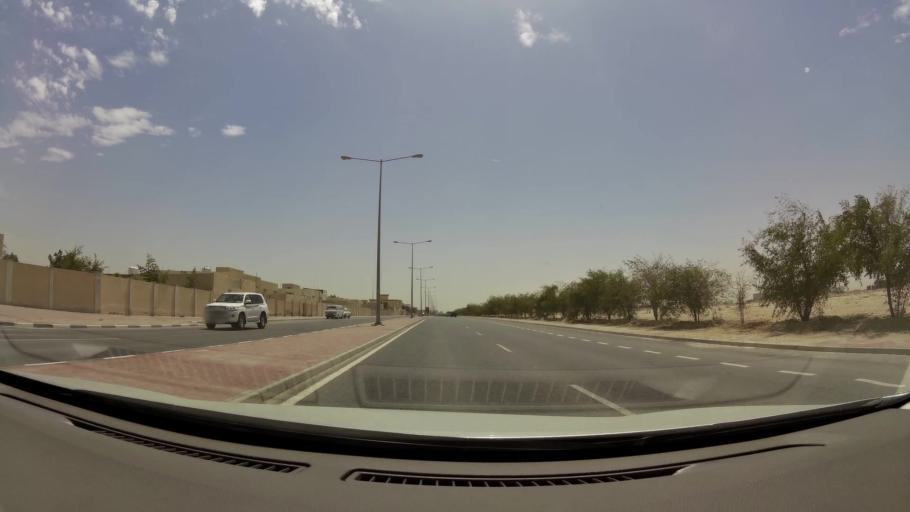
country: QA
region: Baladiyat ar Rayyan
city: Ar Rayyan
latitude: 25.2916
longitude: 51.4066
